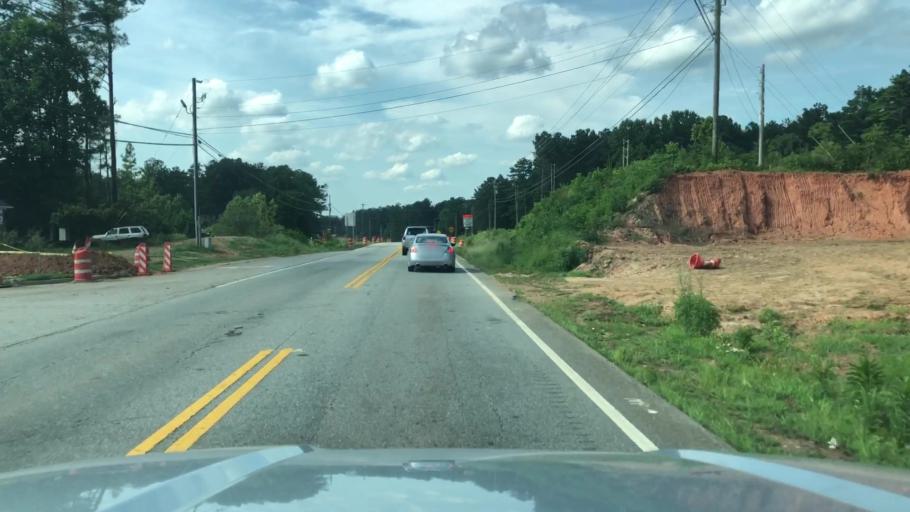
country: US
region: Georgia
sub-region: Douglas County
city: Douglasville
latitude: 33.7735
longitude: -84.7476
